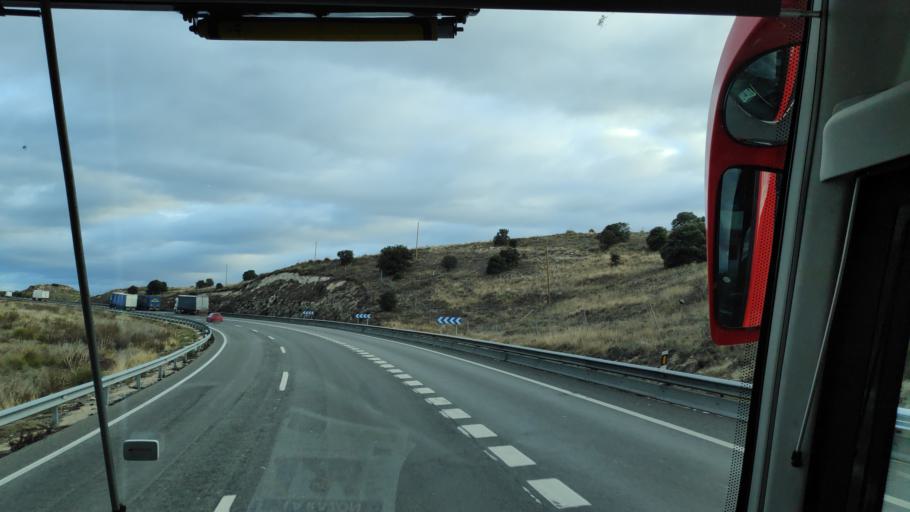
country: ES
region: Madrid
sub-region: Provincia de Madrid
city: Tielmes
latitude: 40.1999
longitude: -3.3144
